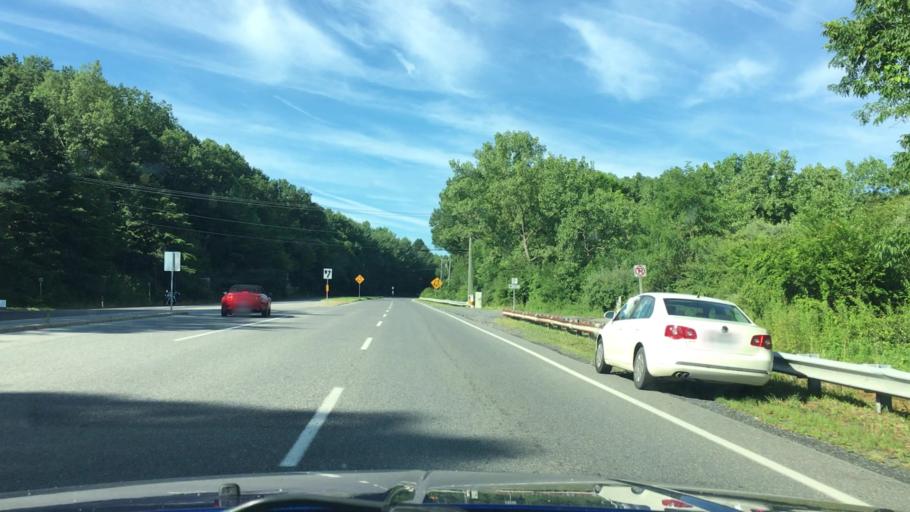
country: US
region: Virginia
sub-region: City of Waynesboro
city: Waynesboro
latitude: 38.0453
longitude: -78.9077
